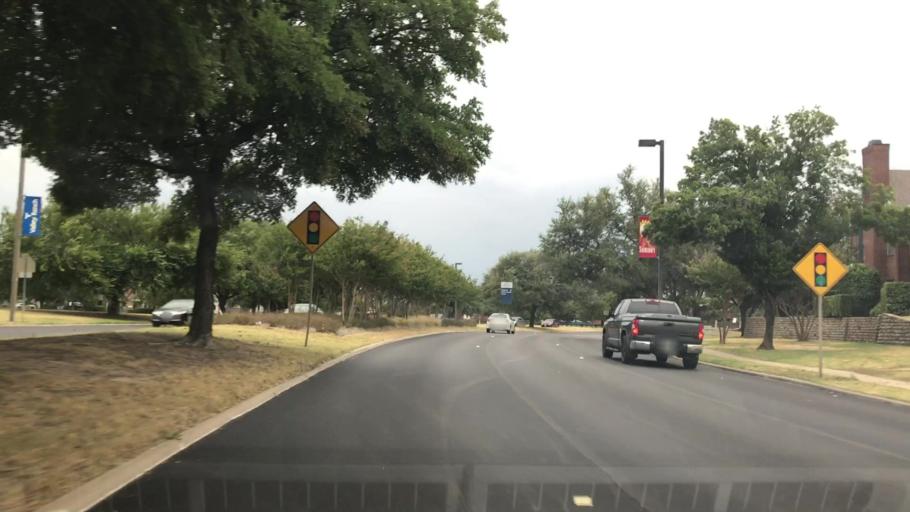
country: US
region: Texas
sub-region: Dallas County
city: Farmers Branch
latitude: 32.9456
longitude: -96.9529
